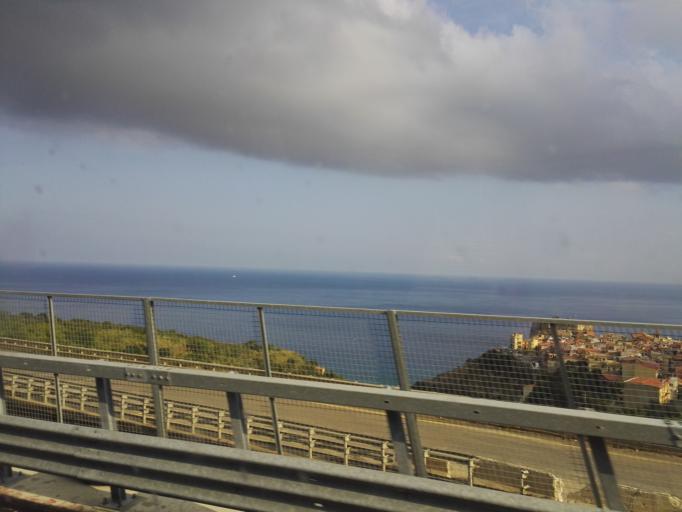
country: IT
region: Calabria
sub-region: Provincia di Reggio Calabria
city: Scilla
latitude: 38.2487
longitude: 15.7159
